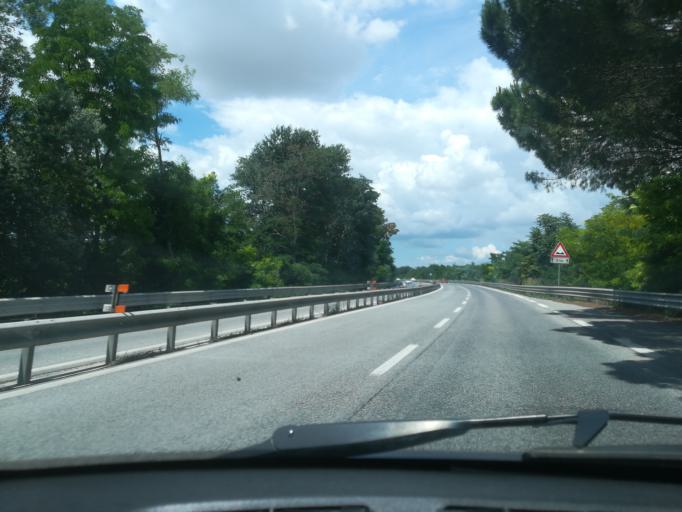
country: IT
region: The Marches
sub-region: Provincia di Macerata
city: Corridonia
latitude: 43.2657
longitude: 13.5445
